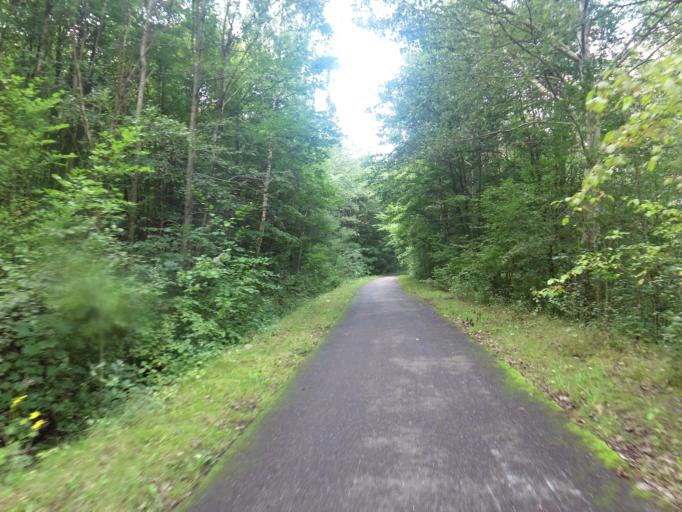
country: NL
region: Limburg
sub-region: Gemeente Heerlen
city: Nieuw-Lotbroek
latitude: 50.9175
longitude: 5.9436
